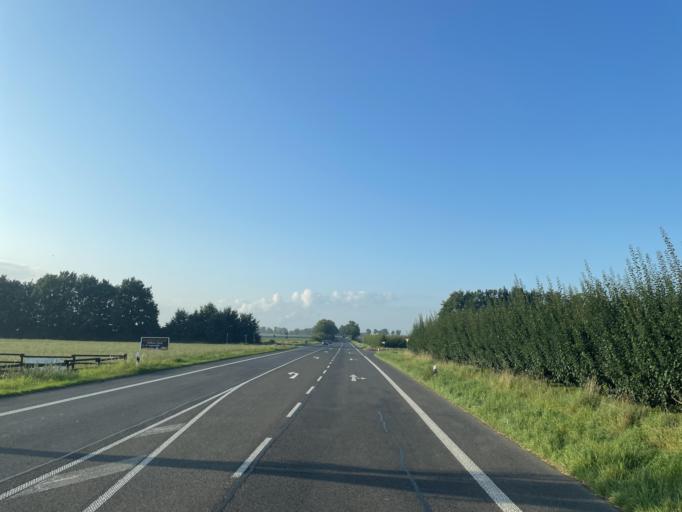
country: DE
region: North Rhine-Westphalia
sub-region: Regierungsbezirk Dusseldorf
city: Neubrueck
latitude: 51.1613
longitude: 6.5932
